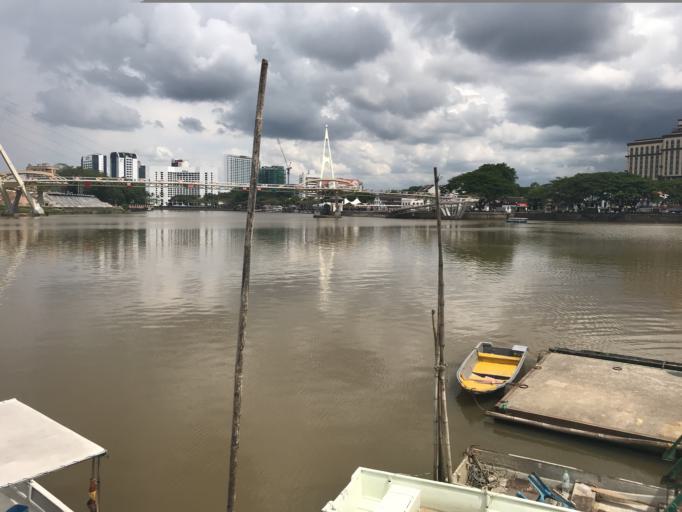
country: MY
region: Sarawak
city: Kuching
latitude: 1.5630
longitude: 110.3443
